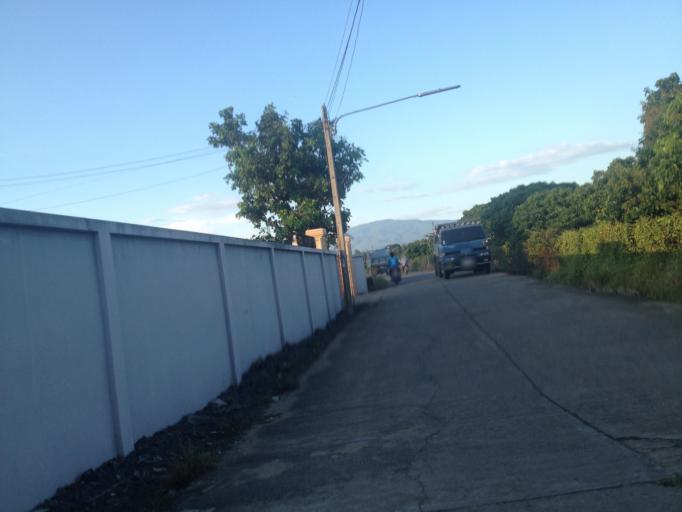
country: TH
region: Chiang Mai
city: San Pa Tong
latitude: 18.6598
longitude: 98.8873
